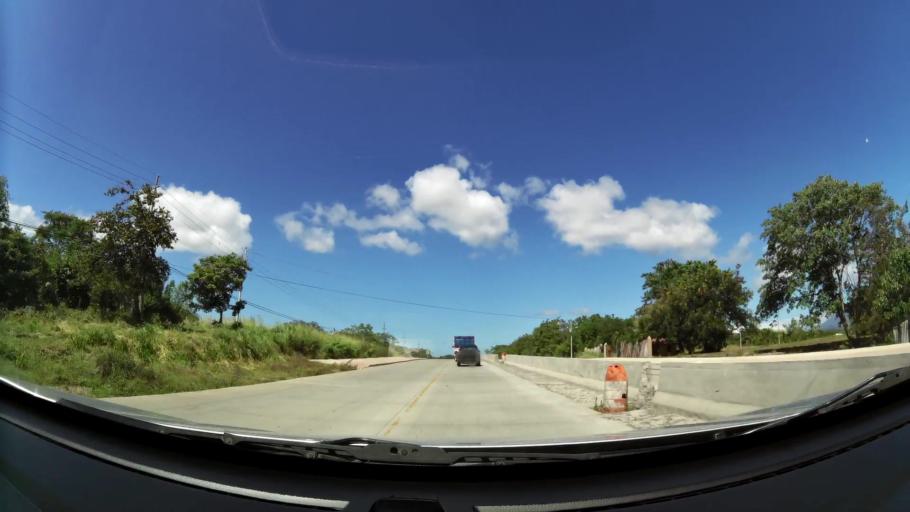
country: CR
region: Guanacaste
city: Bagaces
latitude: 10.5097
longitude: -85.2355
